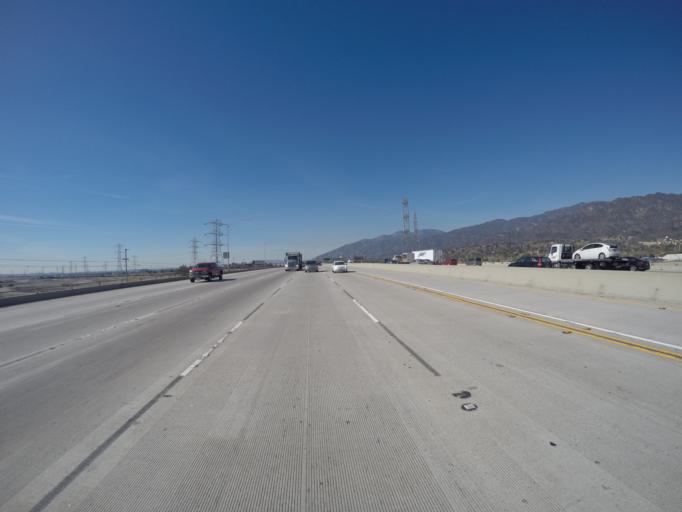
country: US
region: California
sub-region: Los Angeles County
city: Bradbury
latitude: 34.1320
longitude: -117.9495
